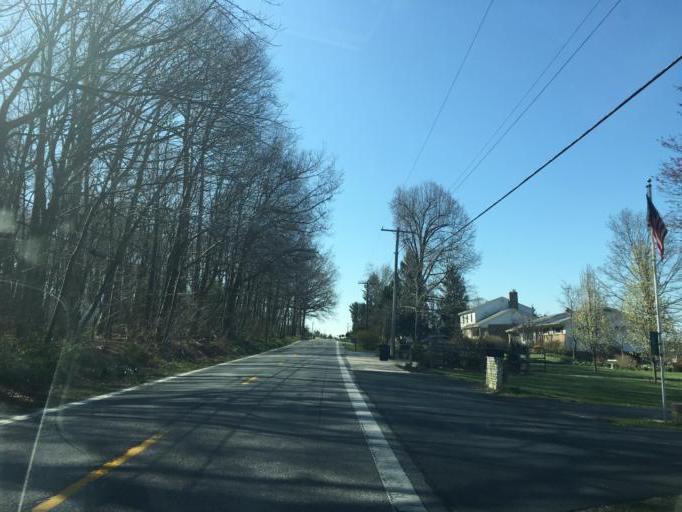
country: US
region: Maryland
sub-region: Washington County
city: Cavetown
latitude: 39.5875
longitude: -77.5576
